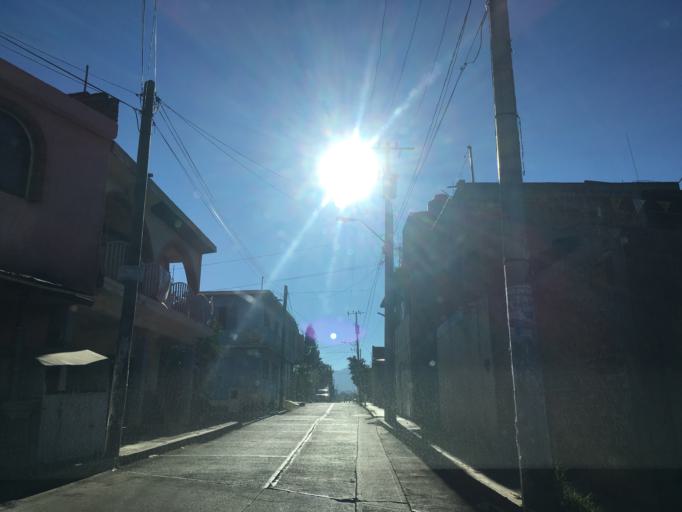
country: MX
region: Michoacan
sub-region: Morelia
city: Montana Monarca (Punta Altozano)
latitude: 19.6589
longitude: -101.1575
